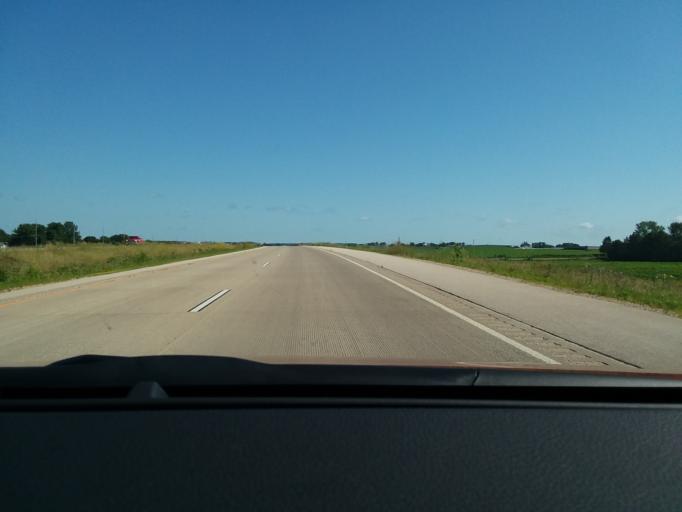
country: US
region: Wisconsin
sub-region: Dane County
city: De Forest
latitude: 43.2355
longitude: -89.3225
